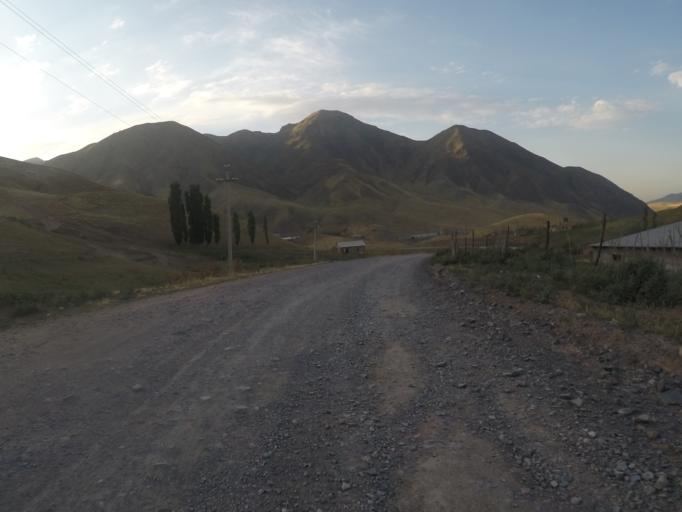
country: KG
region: Chuy
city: Bishkek
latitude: 42.6666
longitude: 74.6476
